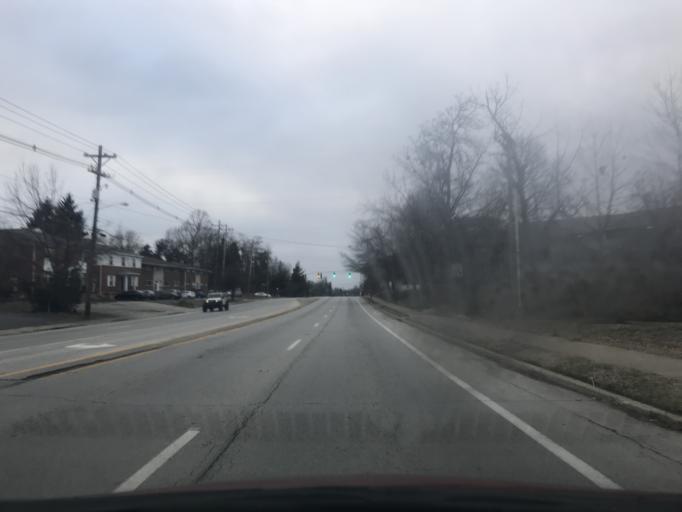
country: US
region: Kentucky
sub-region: Jefferson County
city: Audubon Park
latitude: 38.2130
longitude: -85.7219
